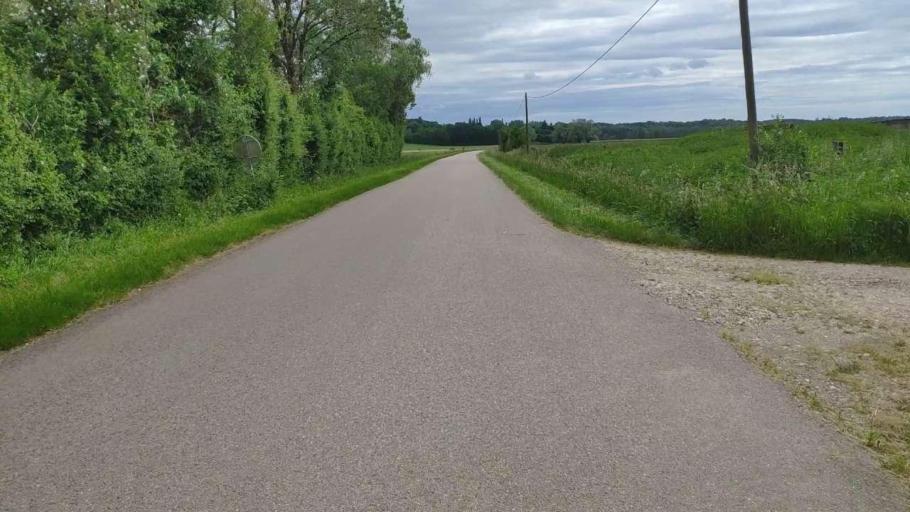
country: FR
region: Franche-Comte
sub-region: Departement du Jura
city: Bletterans
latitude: 46.7372
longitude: 5.4985
